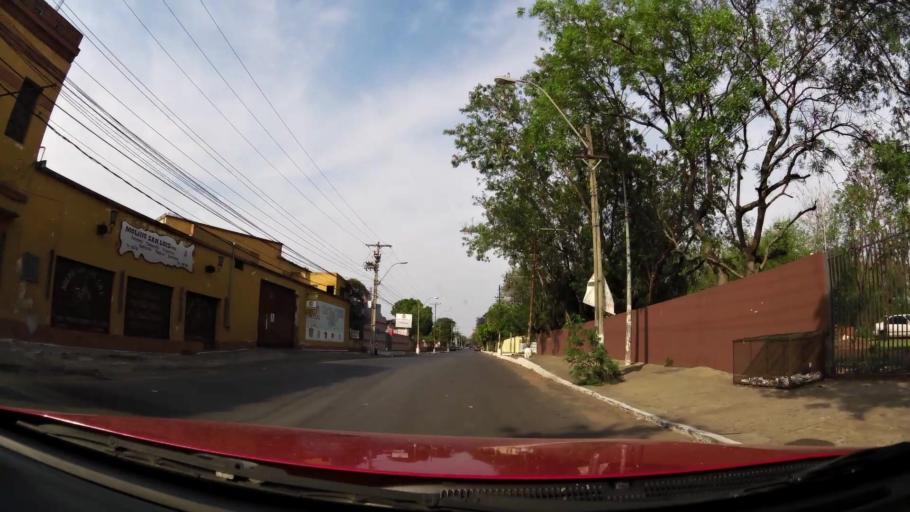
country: PY
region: Asuncion
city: Asuncion
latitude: -25.2756
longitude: -57.6100
